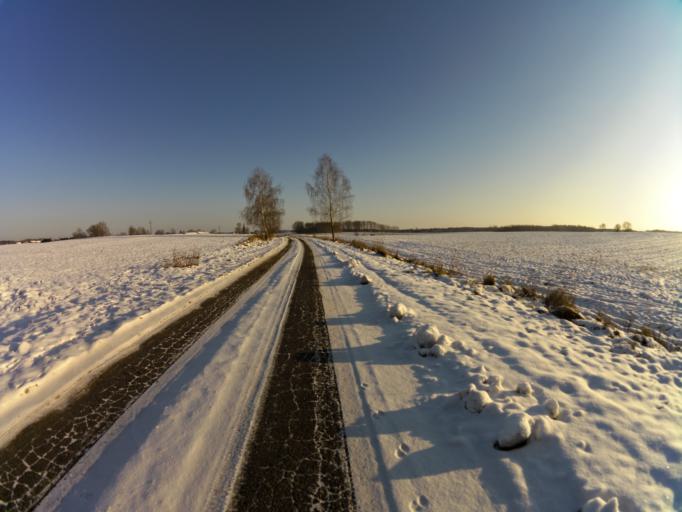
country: PL
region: West Pomeranian Voivodeship
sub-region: Powiat stargardzki
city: Dobrzany
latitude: 53.3259
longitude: 15.4319
